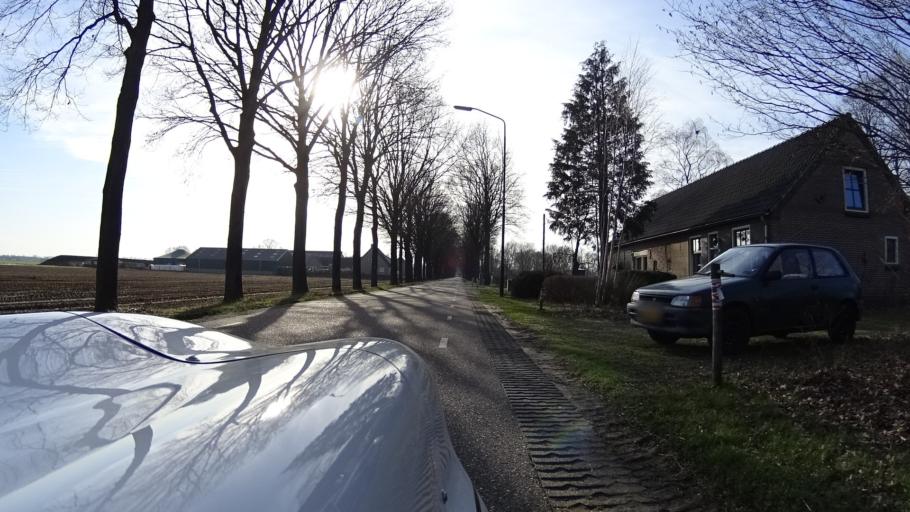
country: NL
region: North Brabant
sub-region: Gemeente Veghel
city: Erp
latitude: 51.5648
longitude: 5.6386
